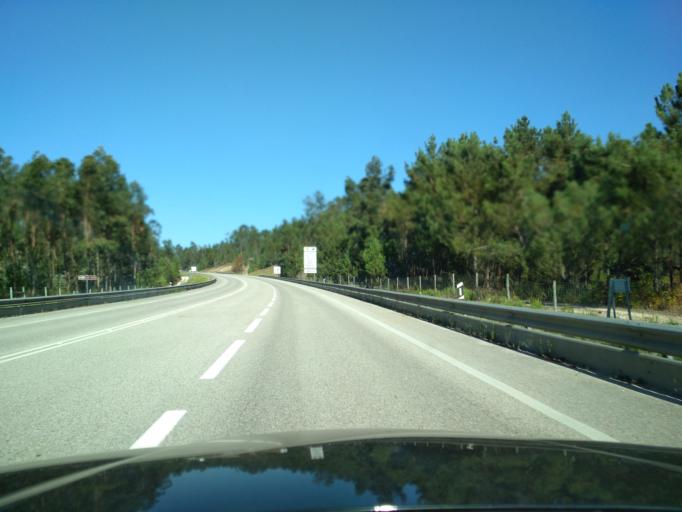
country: PT
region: Leiria
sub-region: Pombal
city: Lourical
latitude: 39.9869
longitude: -8.7673
